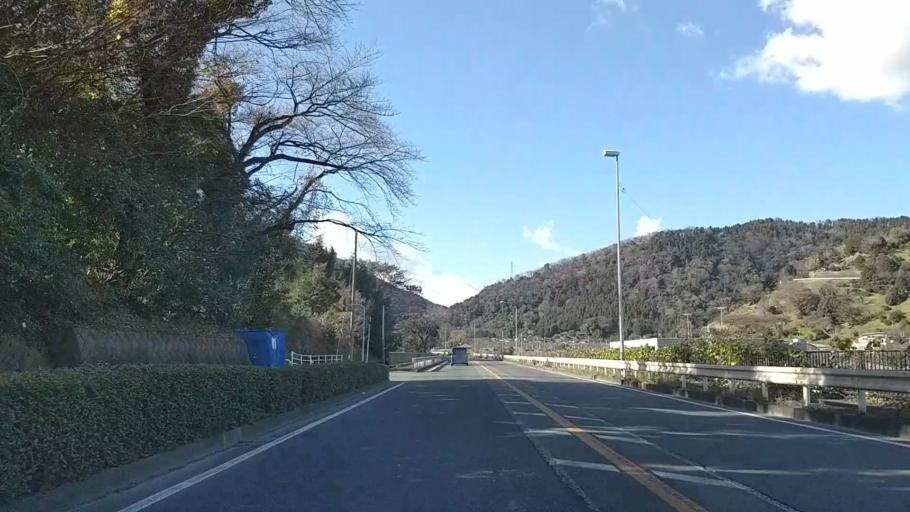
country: JP
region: Kanagawa
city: Odawara
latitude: 35.3592
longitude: 139.0804
